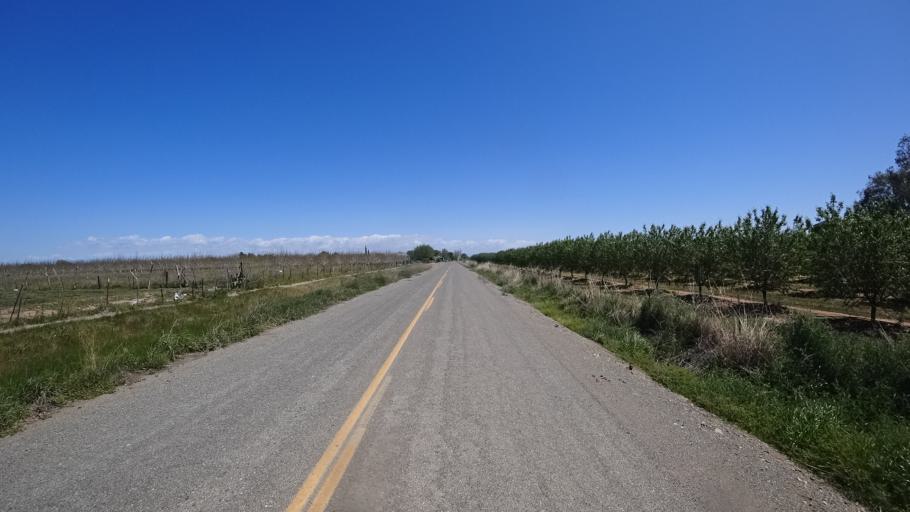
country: US
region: California
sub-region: Glenn County
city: Orland
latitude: 39.7948
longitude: -122.2152
